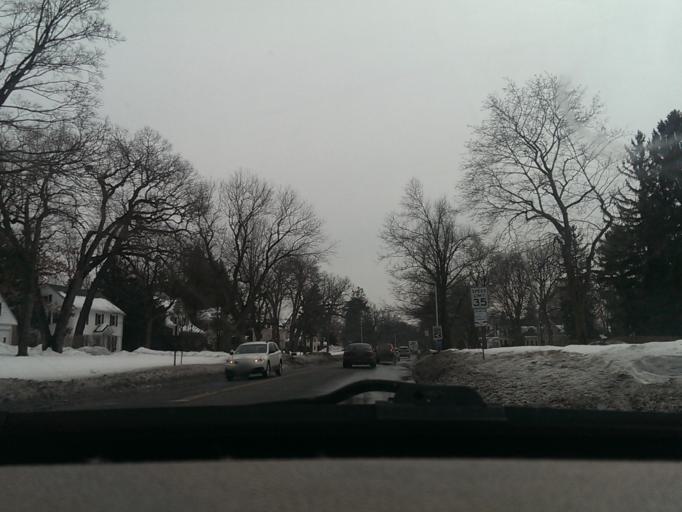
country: US
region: Massachusetts
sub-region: Hampden County
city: Longmeadow
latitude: 42.0706
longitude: -72.5807
